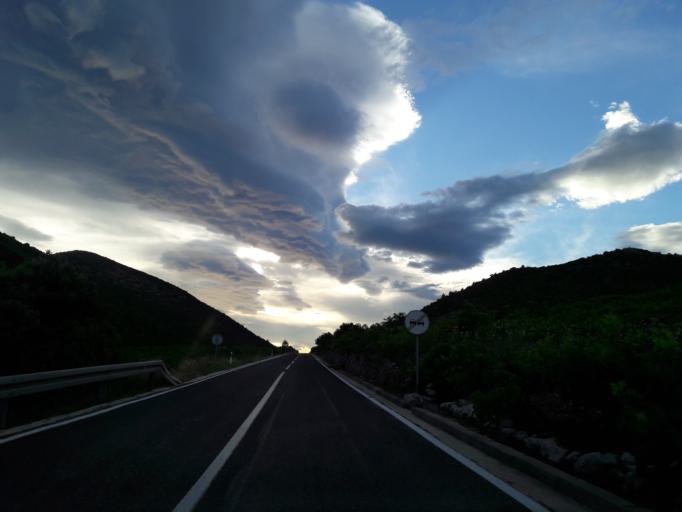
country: HR
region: Dubrovacko-Neretvanska
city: Ston
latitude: 42.8302
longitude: 17.6508
